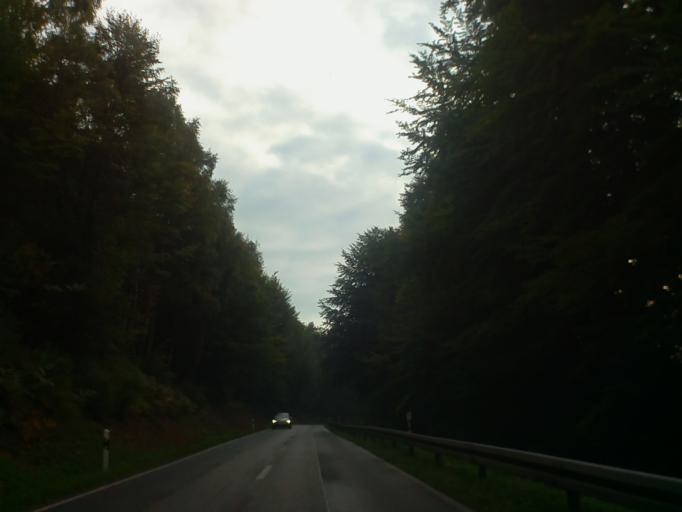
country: DE
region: Hesse
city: Hochst im Odenwald
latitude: 49.7819
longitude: 8.9772
